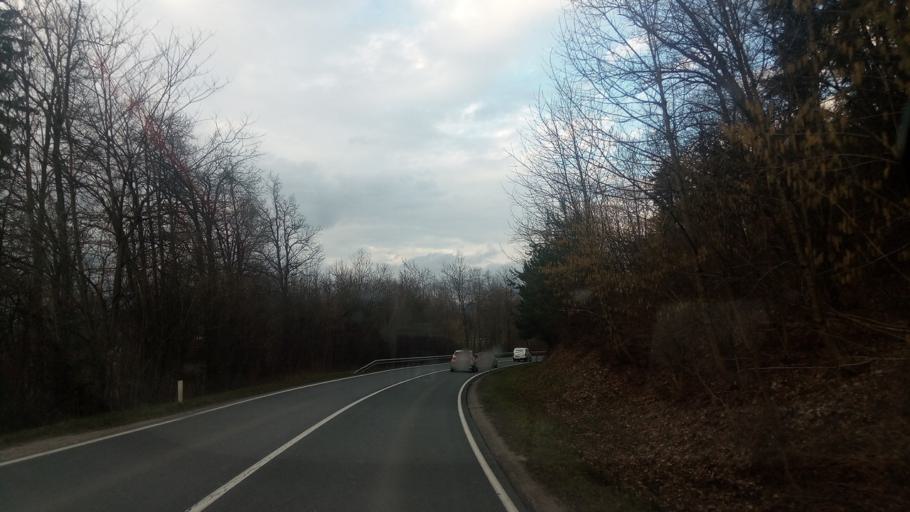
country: SI
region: Domzale
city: Vir
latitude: 46.1412
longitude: 14.6125
